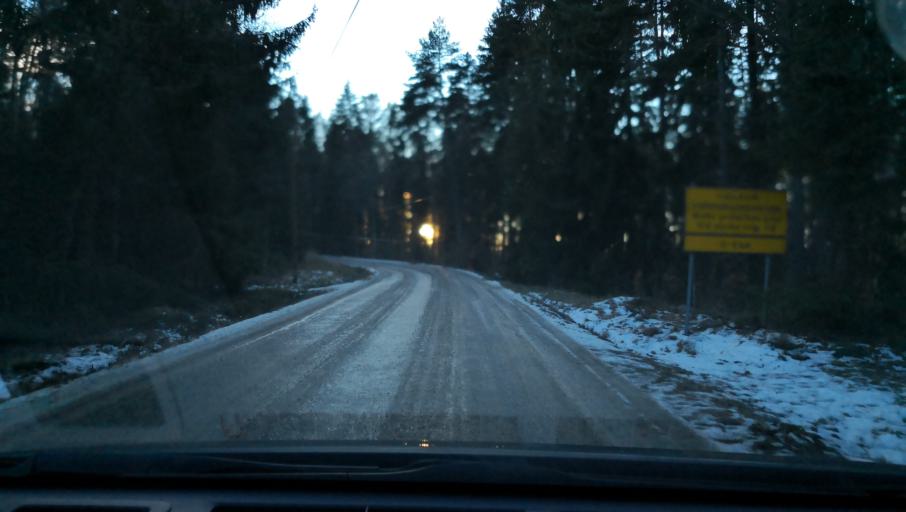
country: SE
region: Vaestmanland
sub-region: Vasteras
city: Tillberga
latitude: 59.7807
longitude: 16.6109
